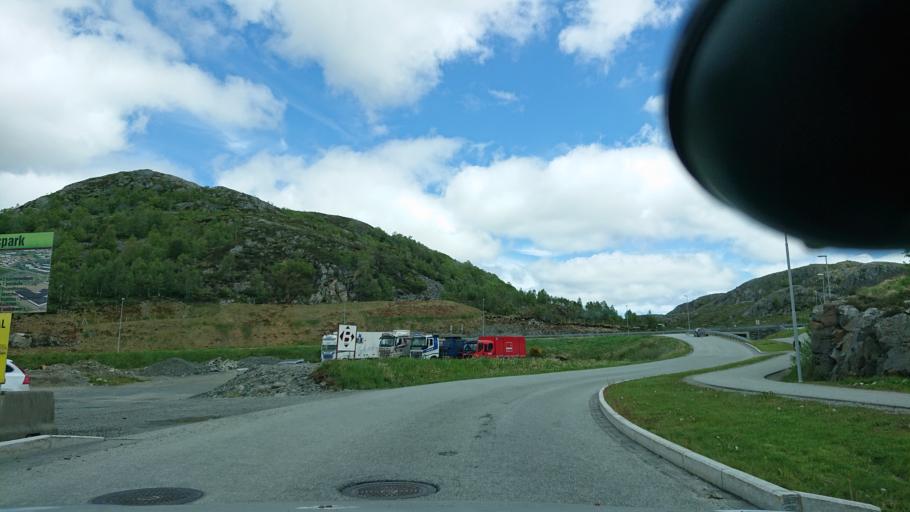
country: NO
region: Rogaland
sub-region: Gjesdal
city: Algard
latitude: 58.7751
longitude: 5.8692
